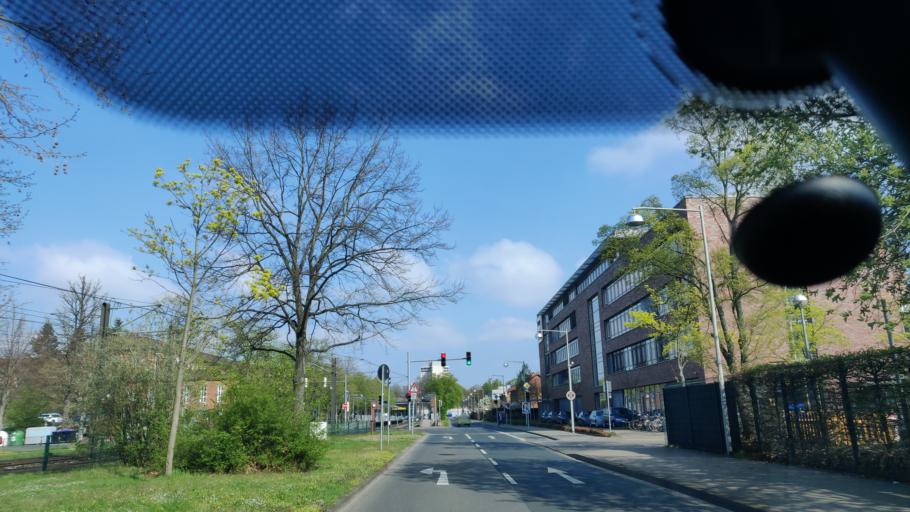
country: DE
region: Lower Saxony
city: Hannover
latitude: 52.3681
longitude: 9.7721
